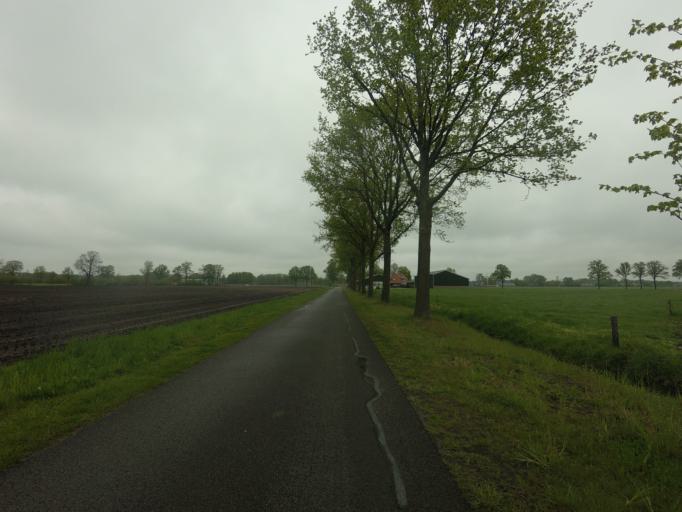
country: NL
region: Overijssel
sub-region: Gemeente Haaksbergen
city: Haaksbergen
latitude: 52.1392
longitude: 6.8084
